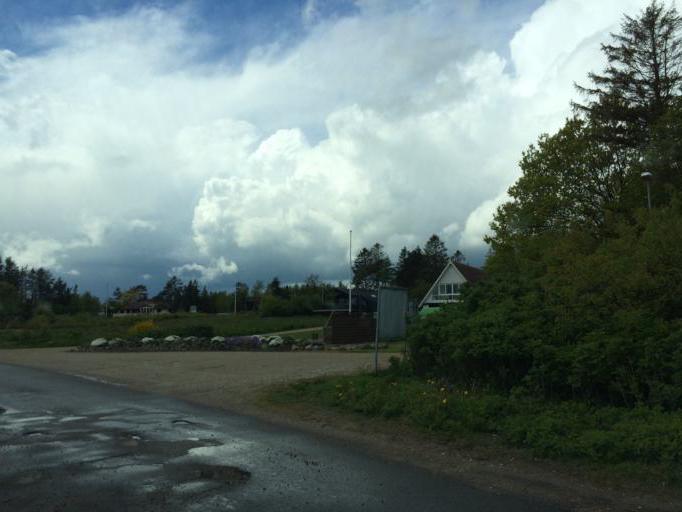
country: DK
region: Central Jutland
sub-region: Skive Kommune
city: Hojslev
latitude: 56.6099
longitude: 9.2904
